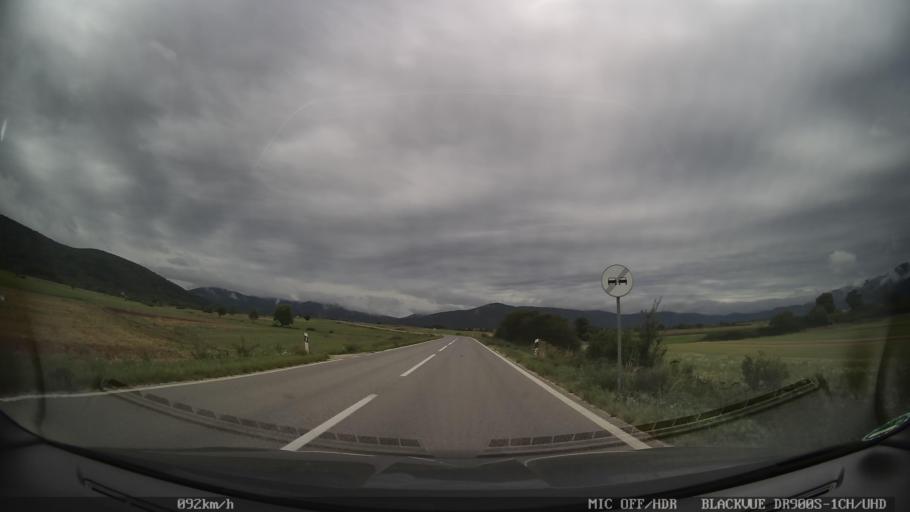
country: HR
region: Licko-Senjska
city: Otocac
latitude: 44.8560
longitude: 15.2797
